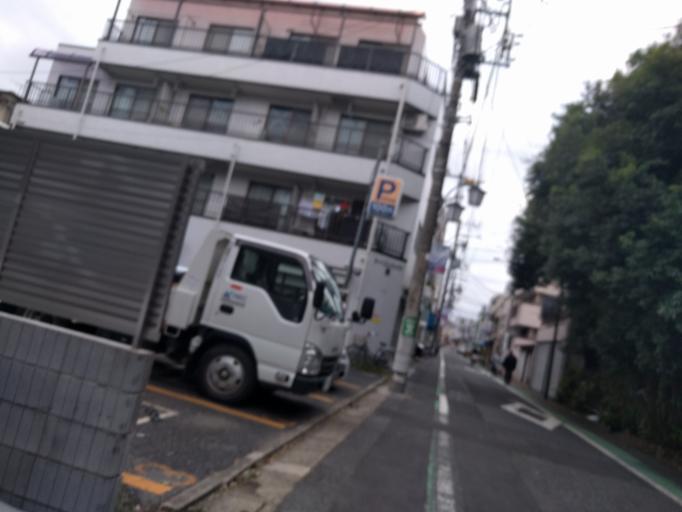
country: JP
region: Tokyo
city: Tokyo
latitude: 35.6426
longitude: 139.6419
